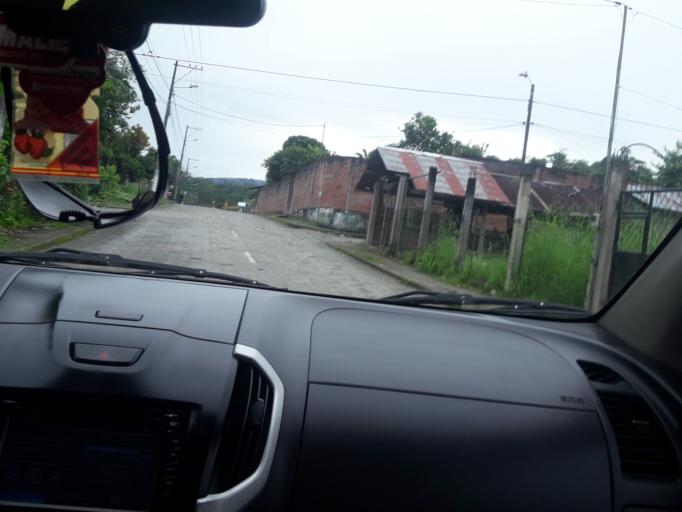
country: EC
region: Napo
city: Tena
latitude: -1.0422
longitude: -77.7923
